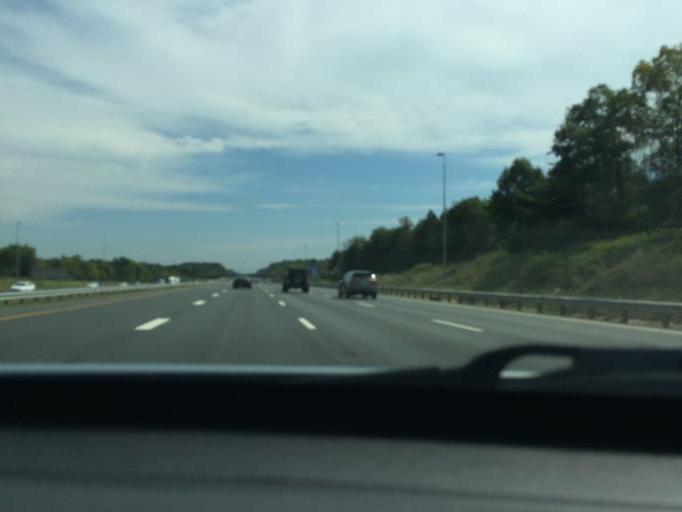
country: US
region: Virginia
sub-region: Prince William County
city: Bull Run
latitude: 38.7989
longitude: -77.5561
